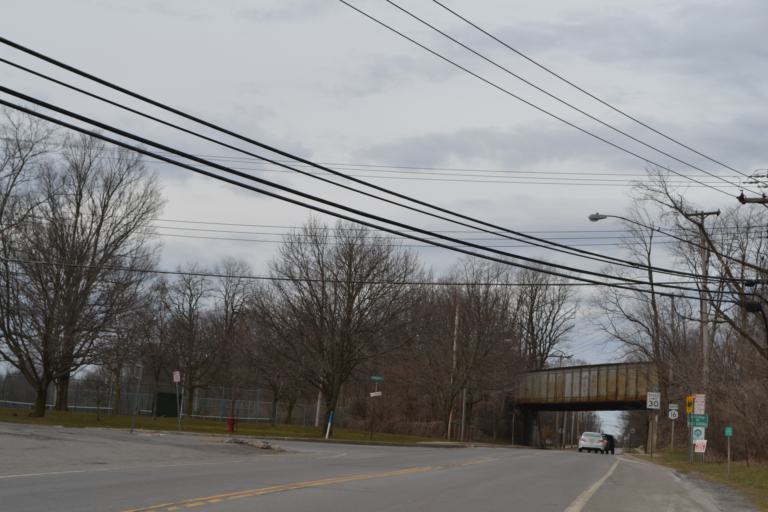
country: US
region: New York
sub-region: Erie County
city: East Aurora
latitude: 42.7568
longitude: -78.6080
